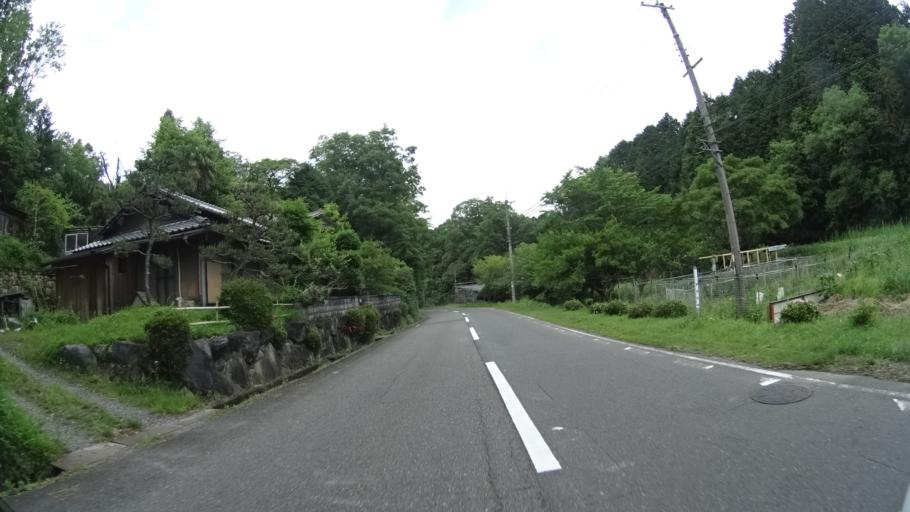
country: JP
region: Nara
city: Nara-shi
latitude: 34.7290
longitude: 135.9087
